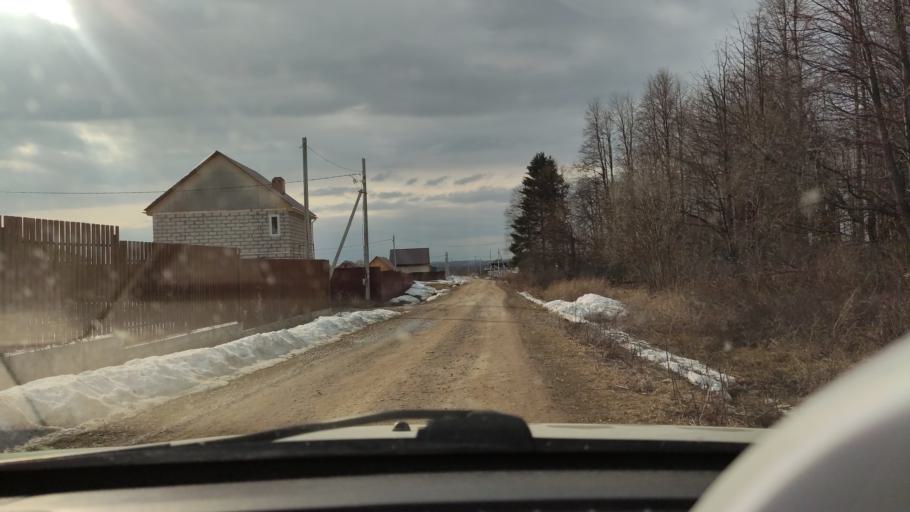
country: RU
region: Perm
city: Ferma
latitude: 57.8842
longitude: 56.3367
